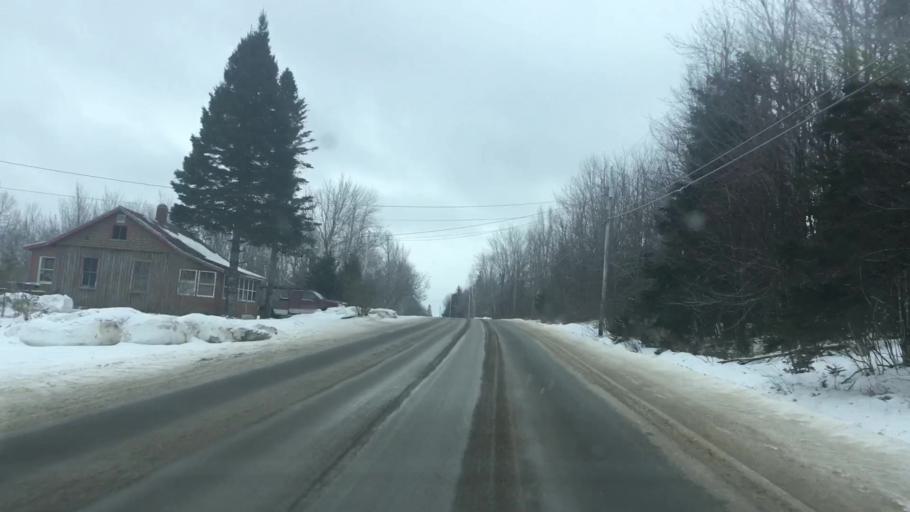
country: US
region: Maine
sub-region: Washington County
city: East Machias
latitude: 44.9875
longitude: -67.4587
